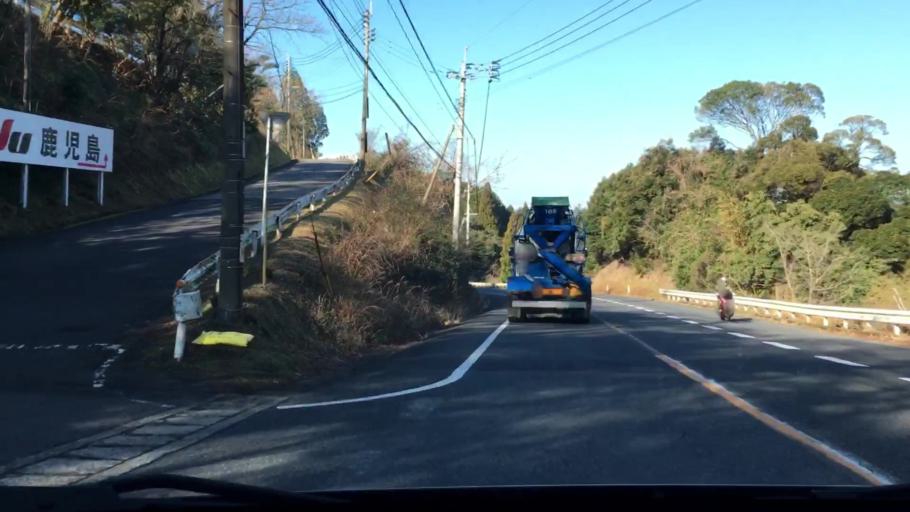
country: JP
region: Kagoshima
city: Kajiki
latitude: 31.7641
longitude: 130.6867
